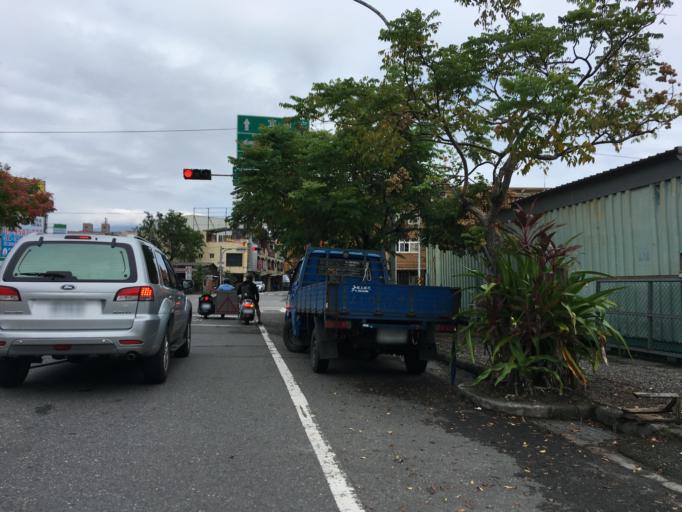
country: TW
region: Taiwan
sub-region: Yilan
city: Yilan
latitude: 24.7420
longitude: 121.7532
